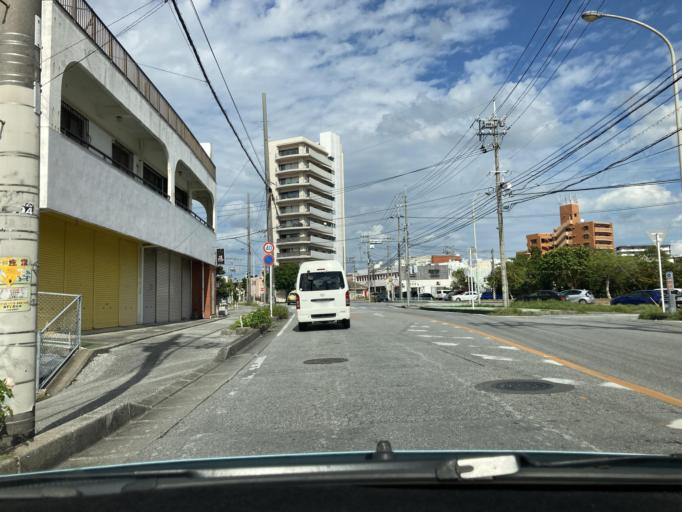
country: JP
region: Okinawa
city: Okinawa
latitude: 26.3218
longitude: 127.7886
